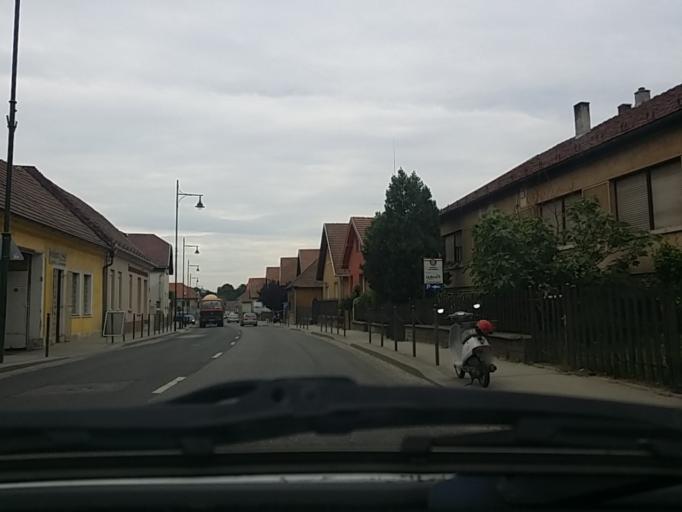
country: HU
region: Pest
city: Pilisvorosvar
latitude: 47.6198
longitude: 18.9120
